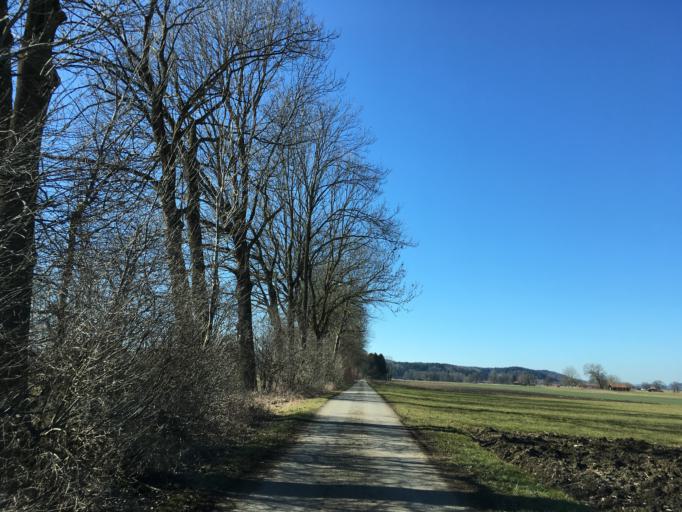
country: DE
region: Bavaria
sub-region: Upper Bavaria
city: Bad Aibling
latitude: 47.8364
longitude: 12.0066
